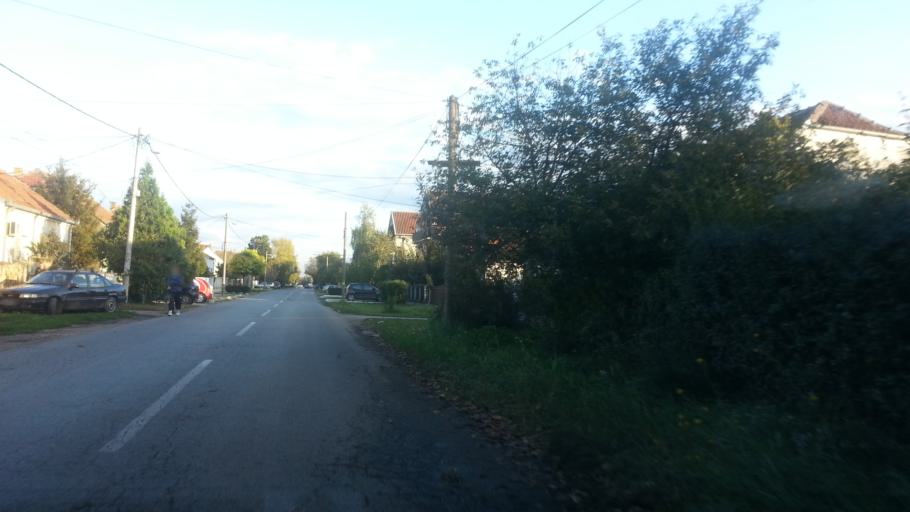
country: RS
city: Novi Banovci
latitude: 44.9021
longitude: 20.2759
